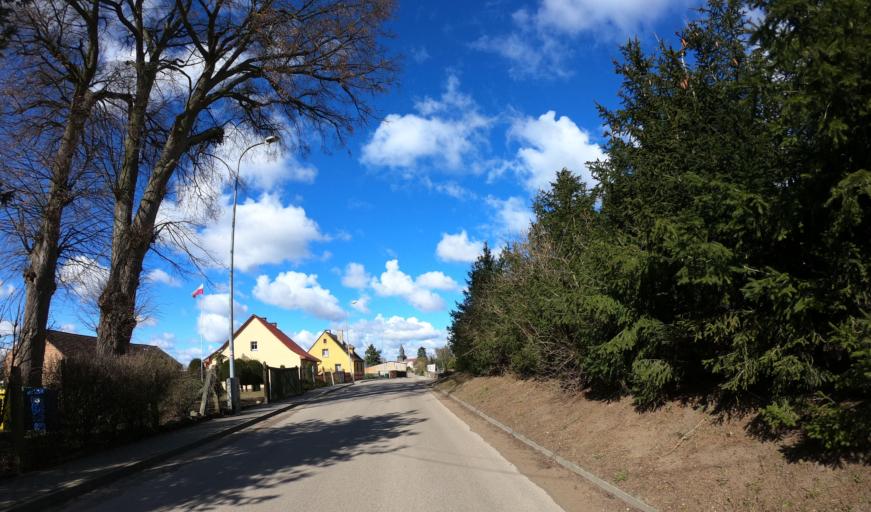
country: PL
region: West Pomeranian Voivodeship
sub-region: Powiat drawski
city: Drawsko Pomorskie
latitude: 53.4897
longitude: 15.8647
